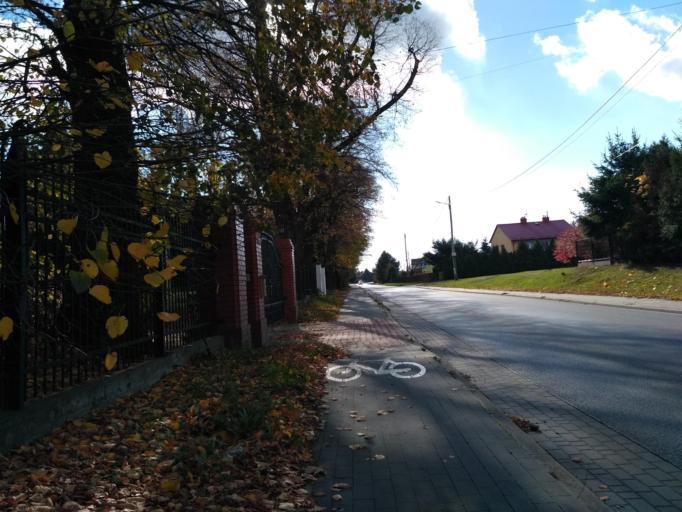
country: PL
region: Subcarpathian Voivodeship
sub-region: Powiat rzeszowski
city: Trzciana
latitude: 50.1143
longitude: 21.8592
